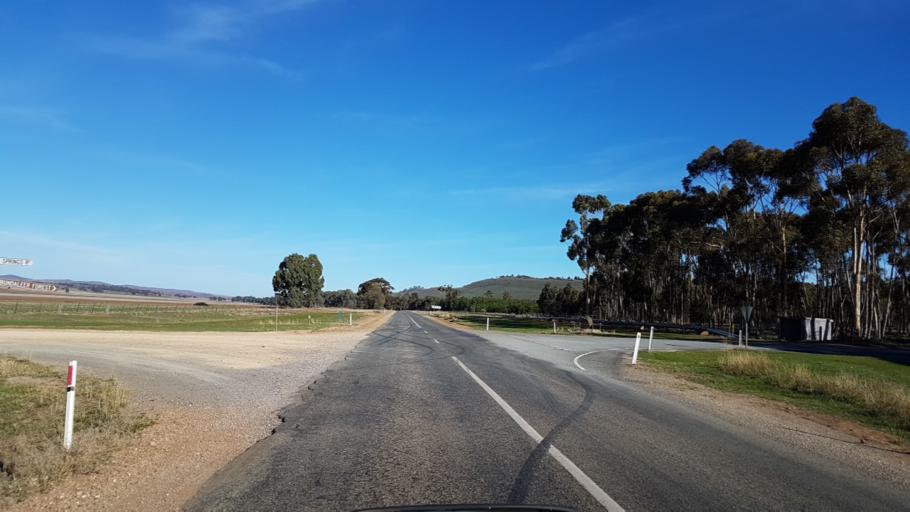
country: AU
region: South Australia
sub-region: Northern Areas
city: Jamestown
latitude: -33.2781
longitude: 138.5763
